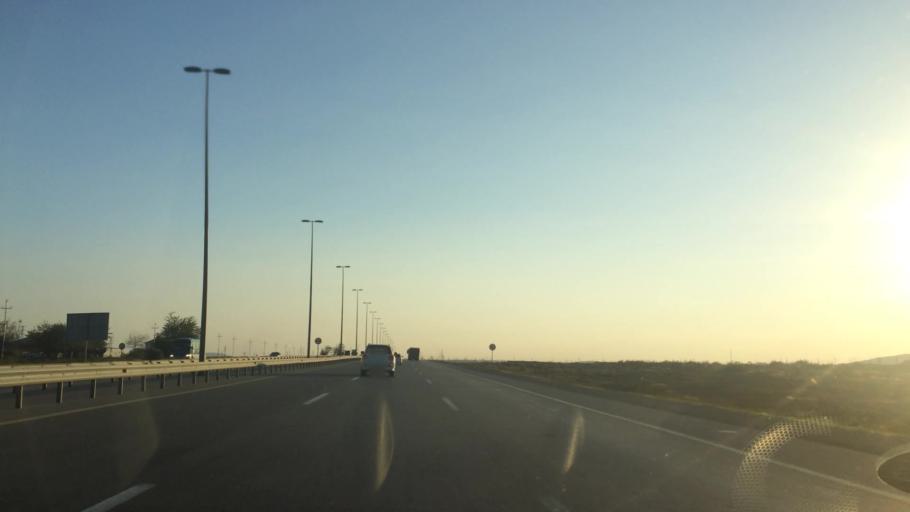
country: AZ
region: Baki
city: Qobustan
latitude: 39.9895
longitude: 49.4292
